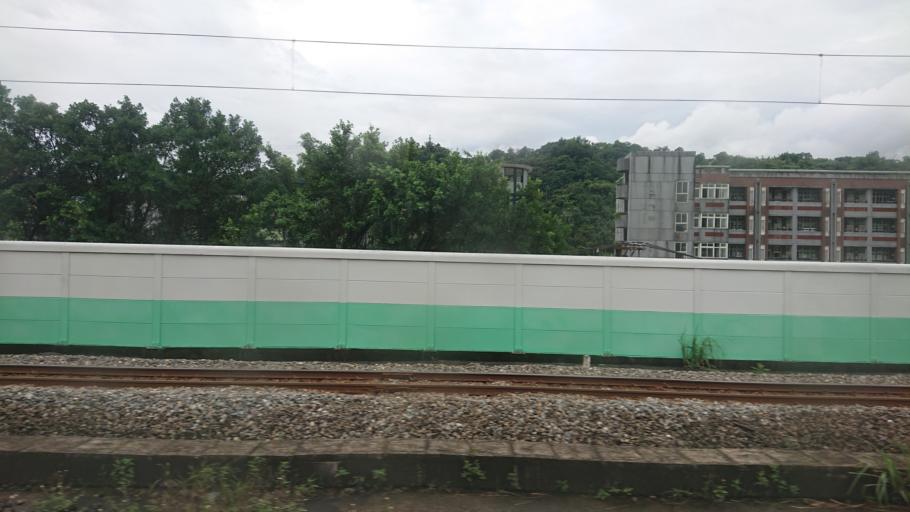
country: TW
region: Taiwan
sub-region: Keelung
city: Keelung
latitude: 25.0940
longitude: 121.7155
